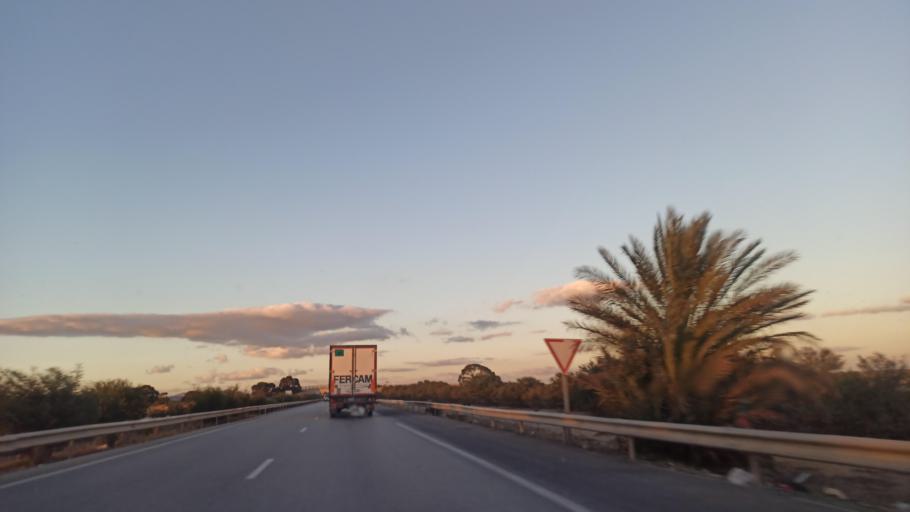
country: TN
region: Susah
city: Harqalah
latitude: 36.1152
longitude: 10.4052
